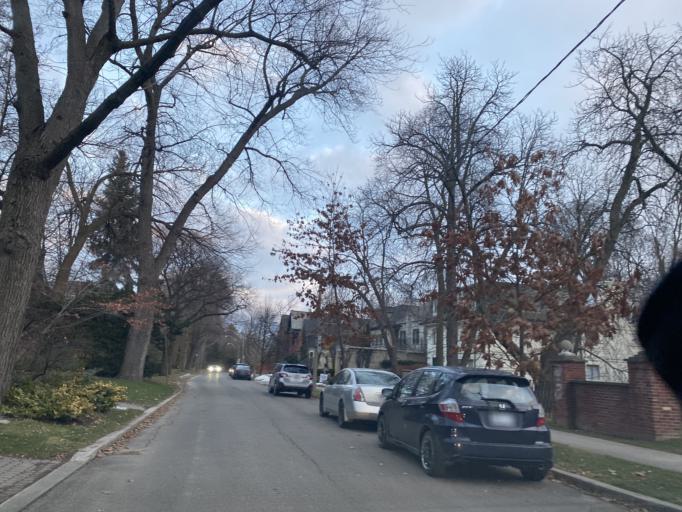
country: CA
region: Ontario
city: Toronto
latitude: 43.6742
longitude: -79.3710
